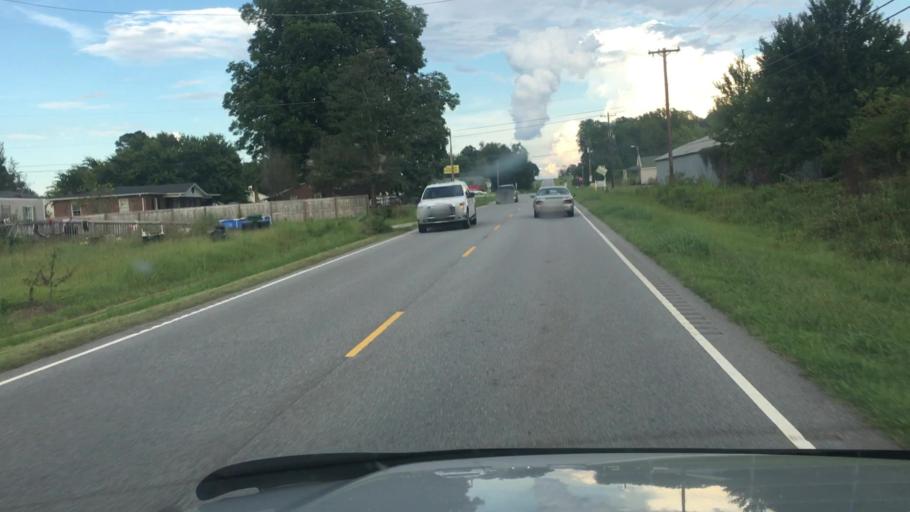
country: US
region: South Carolina
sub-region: Spartanburg County
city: Mayo
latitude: 35.1276
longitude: -81.7842
